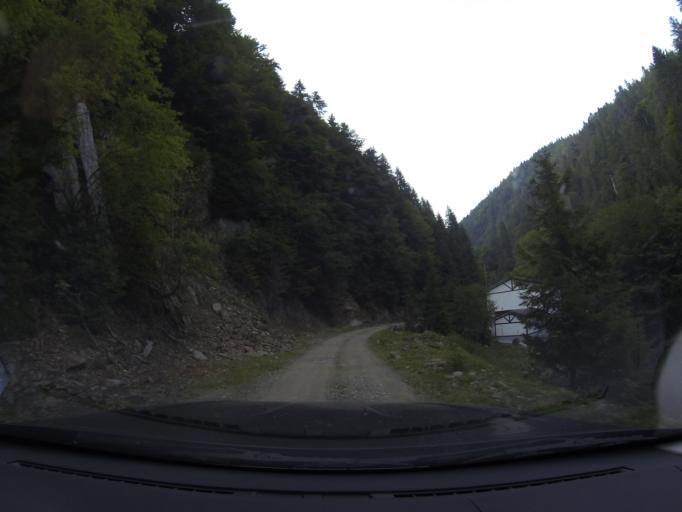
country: RO
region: Arges
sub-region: Comuna Arefu
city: Arefu
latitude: 45.5192
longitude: 24.6789
